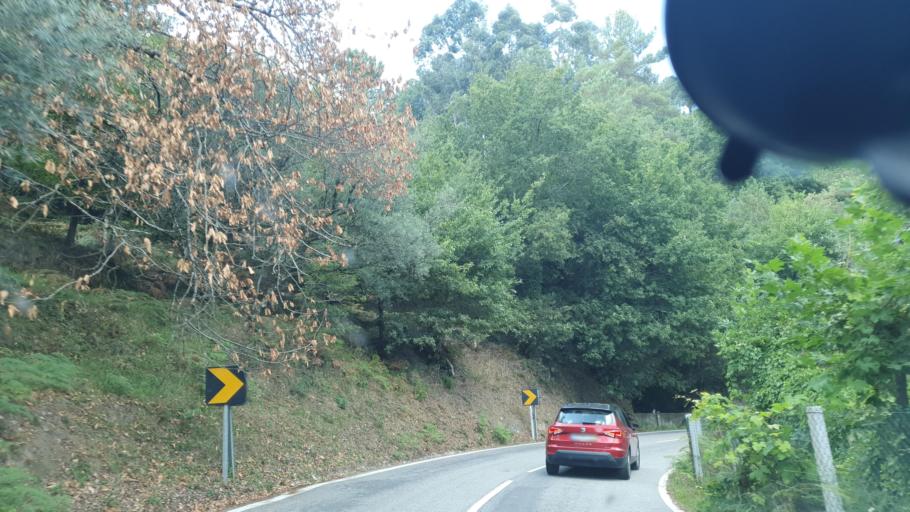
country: PT
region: Braga
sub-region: Vieira do Minho
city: Real
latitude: 41.7131
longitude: -8.2191
